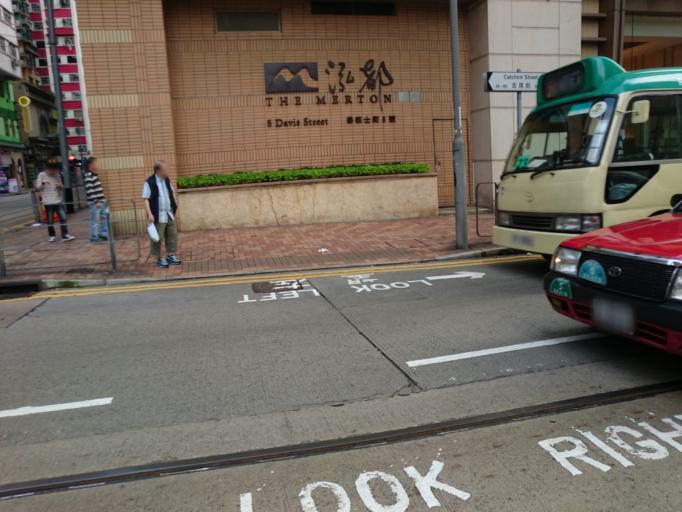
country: HK
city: Hong Kong
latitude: 22.2831
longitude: 114.1266
